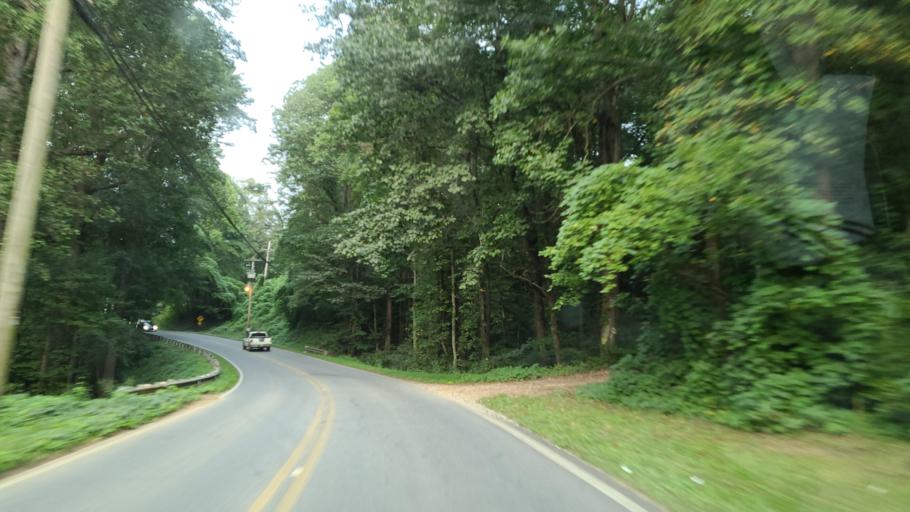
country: US
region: Georgia
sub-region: Fannin County
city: Blue Ridge
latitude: 34.8722
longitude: -84.3334
